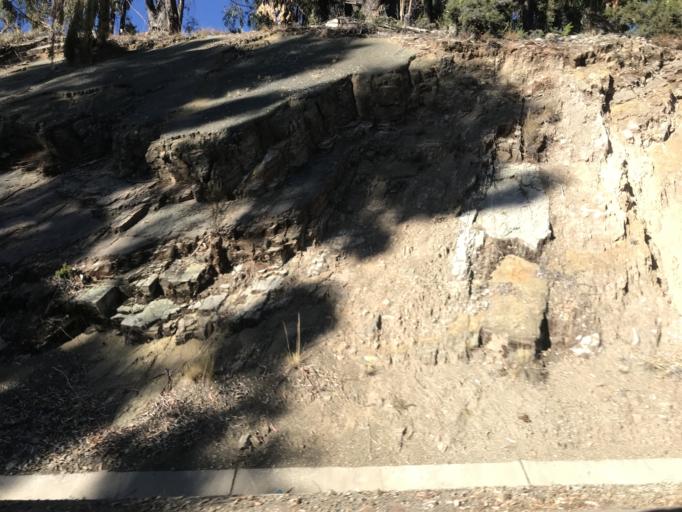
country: BO
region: La Paz
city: San Pedro
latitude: -16.2241
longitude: -68.8549
